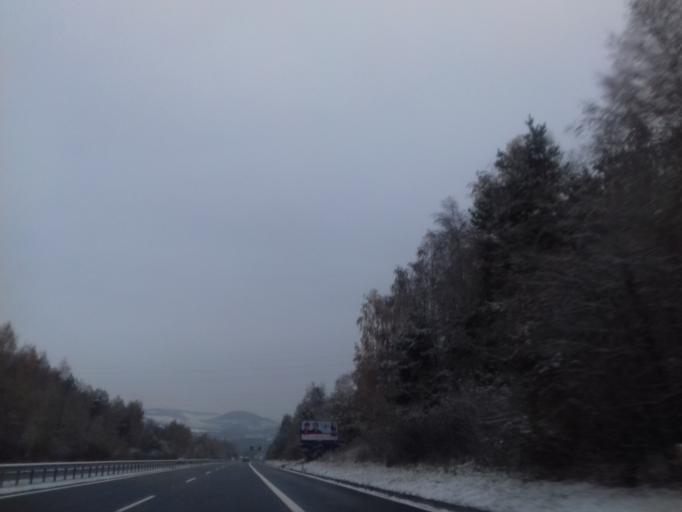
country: CZ
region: Central Bohemia
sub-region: Okres Beroun
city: Beroun
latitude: 49.9696
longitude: 14.0994
